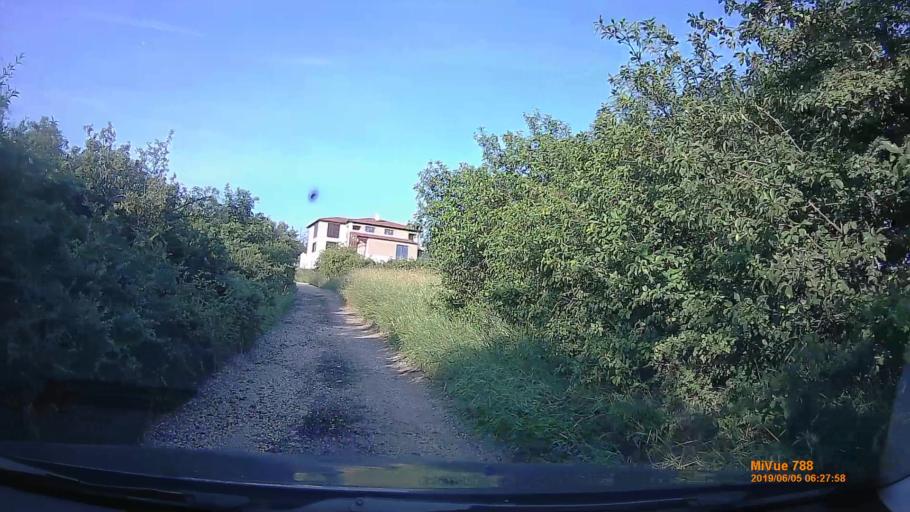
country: HU
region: Pest
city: Urom
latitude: 47.5786
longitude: 19.0304
